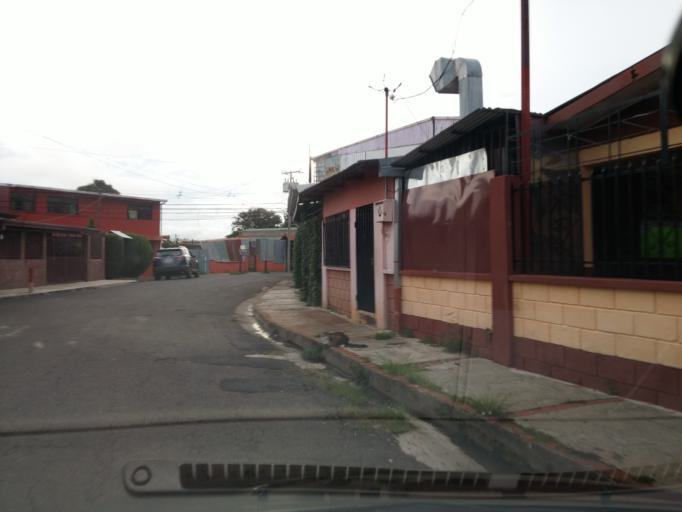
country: CR
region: Heredia
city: Heredia
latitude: 10.0100
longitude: -84.1169
